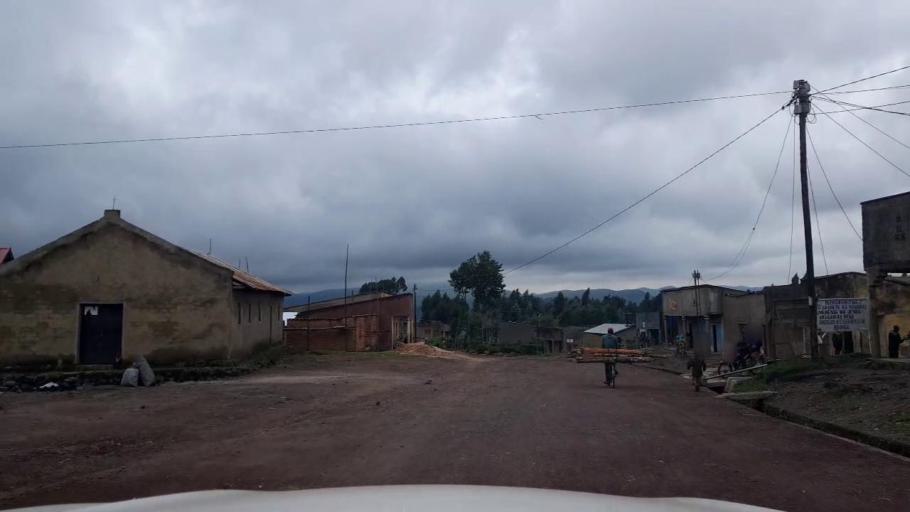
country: RW
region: Northern Province
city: Musanze
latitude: -1.5958
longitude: 29.4524
